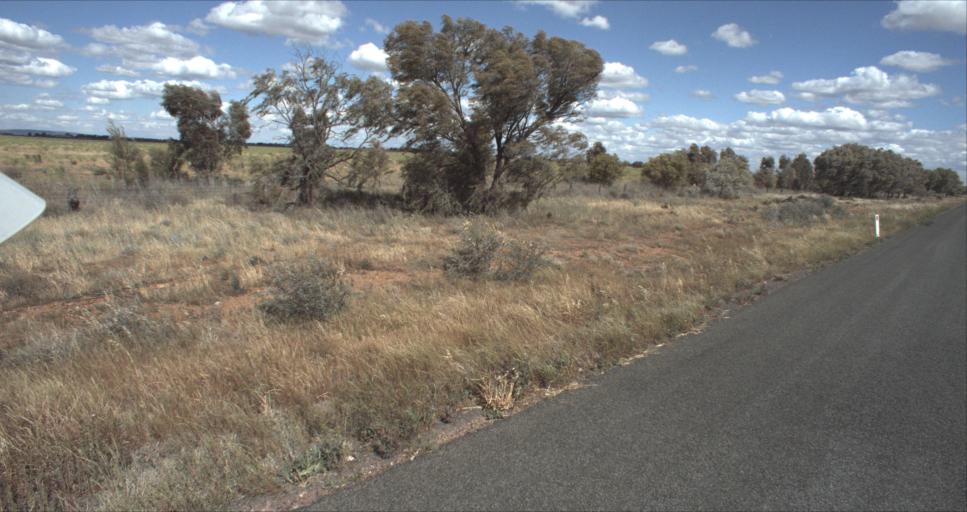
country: AU
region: New South Wales
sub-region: Leeton
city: Leeton
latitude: -34.4351
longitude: 146.2575
